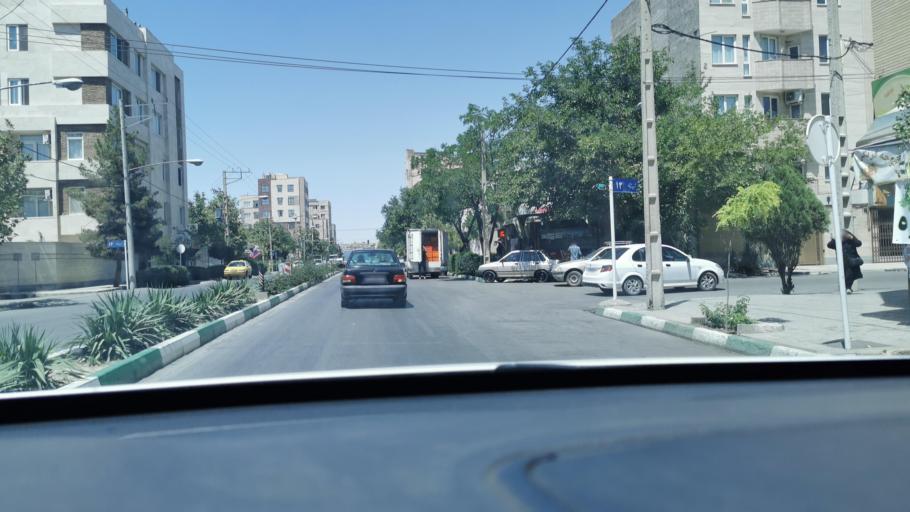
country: IR
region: Razavi Khorasan
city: Mashhad
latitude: 36.3406
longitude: 59.4836
